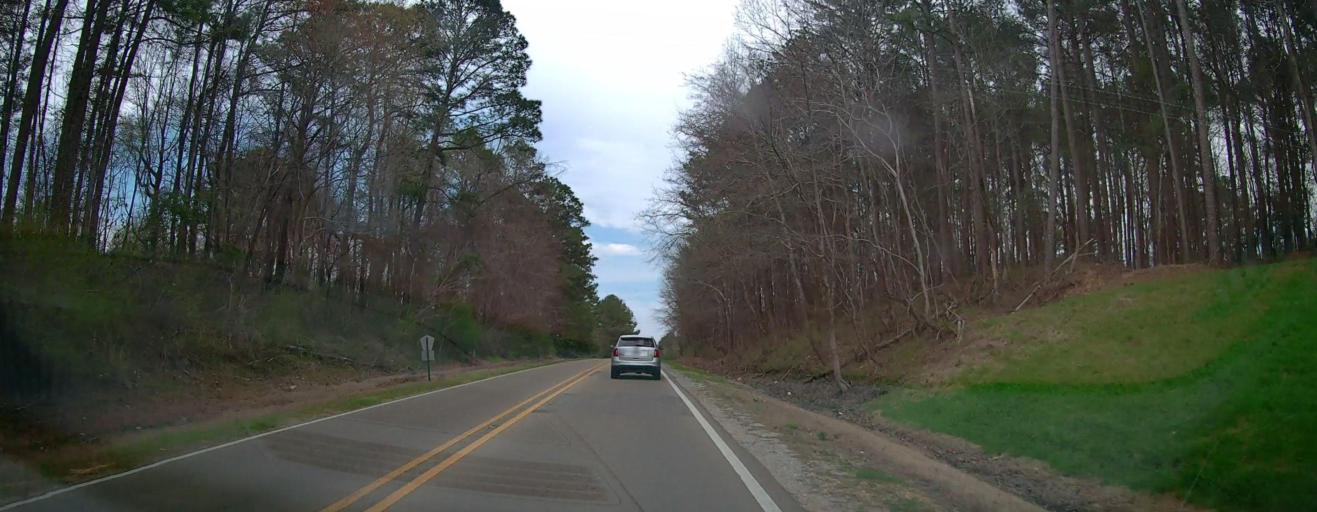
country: US
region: Mississippi
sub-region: Lee County
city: Plantersville
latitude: 34.2664
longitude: -88.5883
